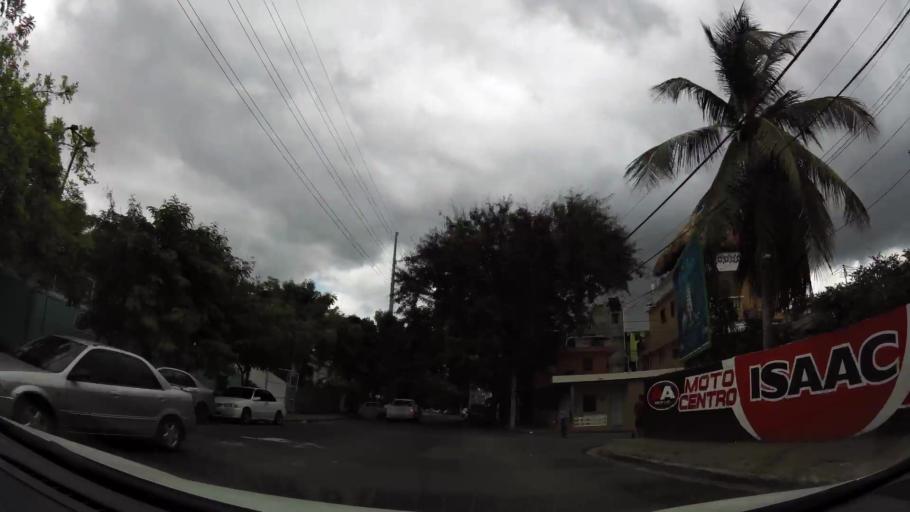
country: DO
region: Nacional
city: Bella Vista
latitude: 18.4520
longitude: -69.9338
